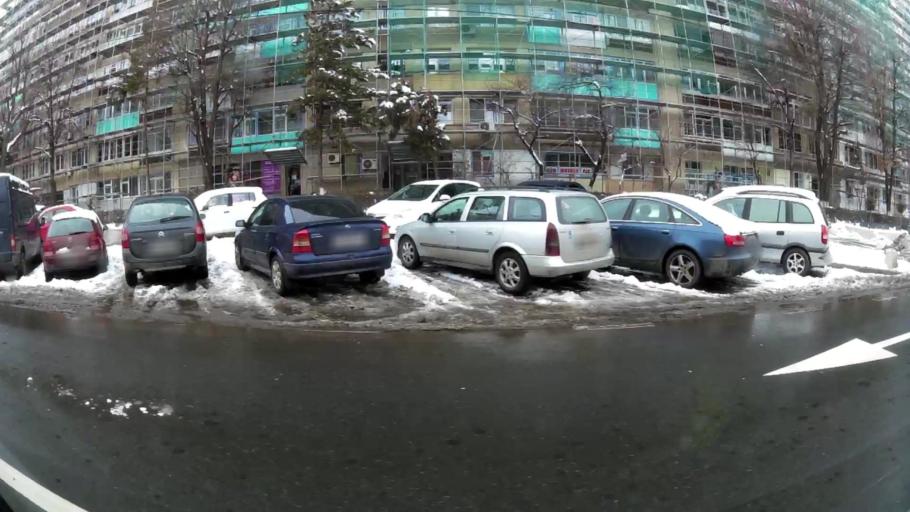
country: RO
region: Bucuresti
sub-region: Municipiul Bucuresti
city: Bucuresti
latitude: 44.3853
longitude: 26.1157
